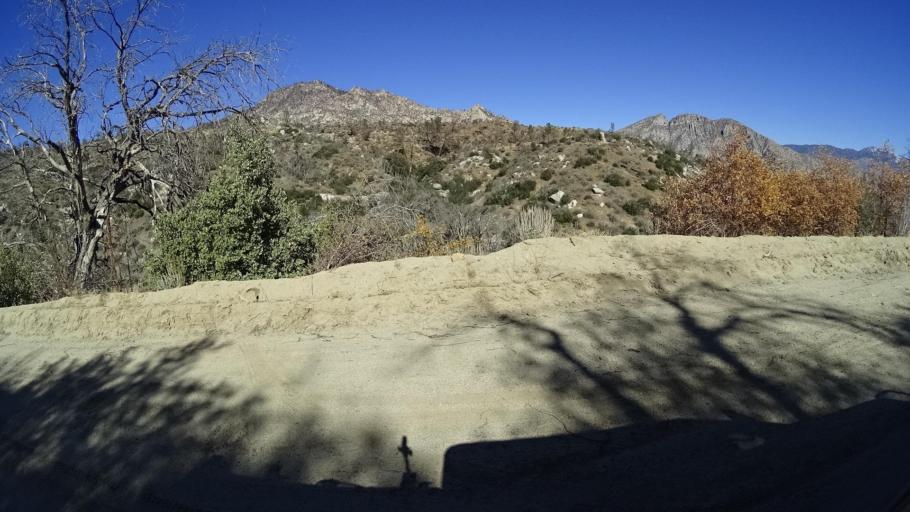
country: US
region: California
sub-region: Kern County
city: Alta Sierra
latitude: 35.7101
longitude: -118.5127
